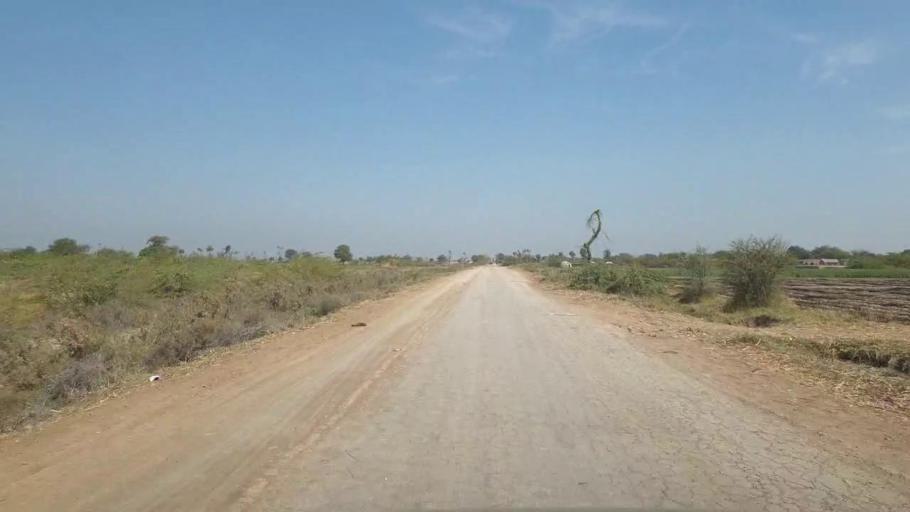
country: PK
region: Sindh
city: Samaro
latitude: 25.3353
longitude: 69.2467
